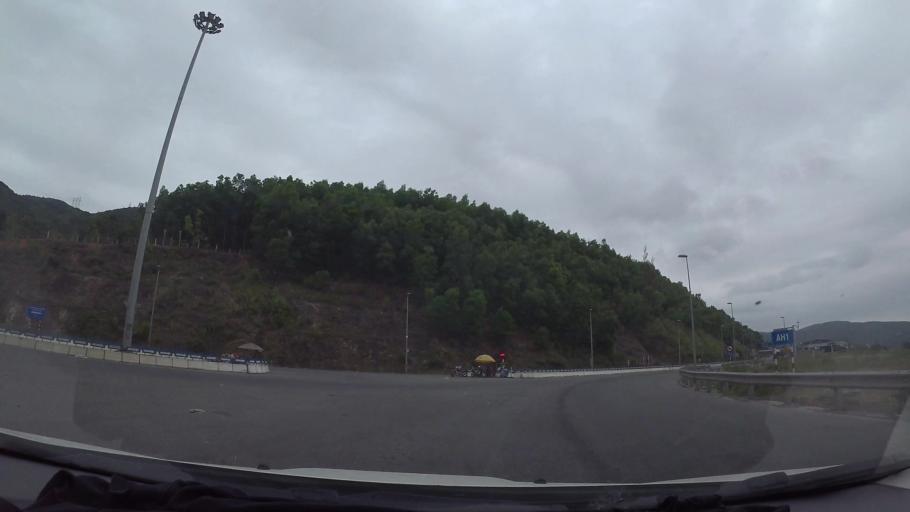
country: VN
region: Da Nang
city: Lien Chieu
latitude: 16.1311
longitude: 108.1054
